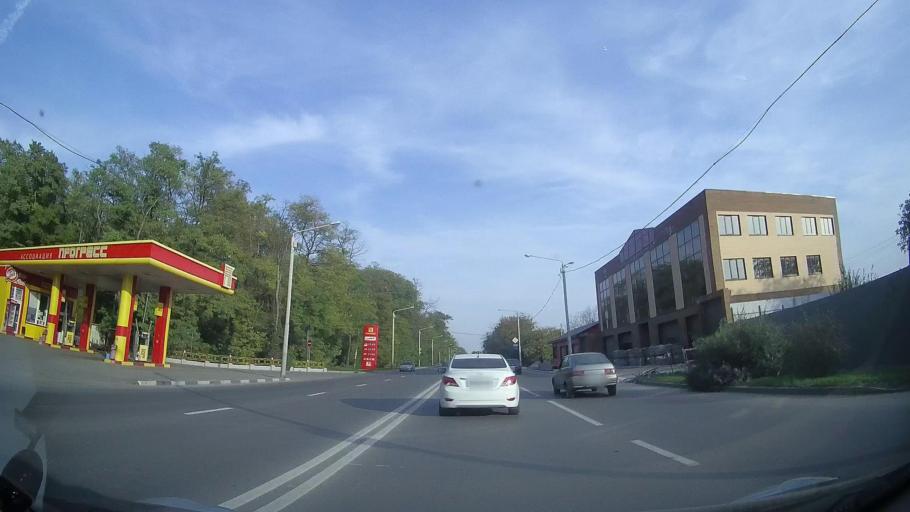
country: RU
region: Rostov
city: Imeni Chkalova
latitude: 47.2761
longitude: 39.7876
